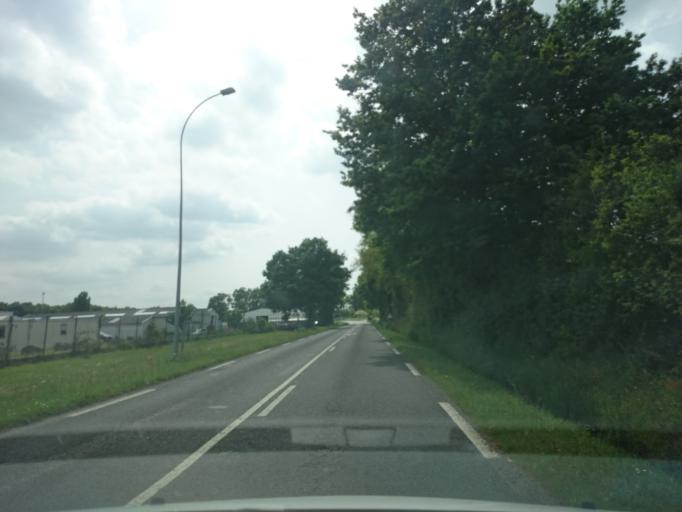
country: FR
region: Pays de la Loire
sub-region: Departement de la Loire-Atlantique
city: La Chevroliere
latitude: 47.1023
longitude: -1.5990
